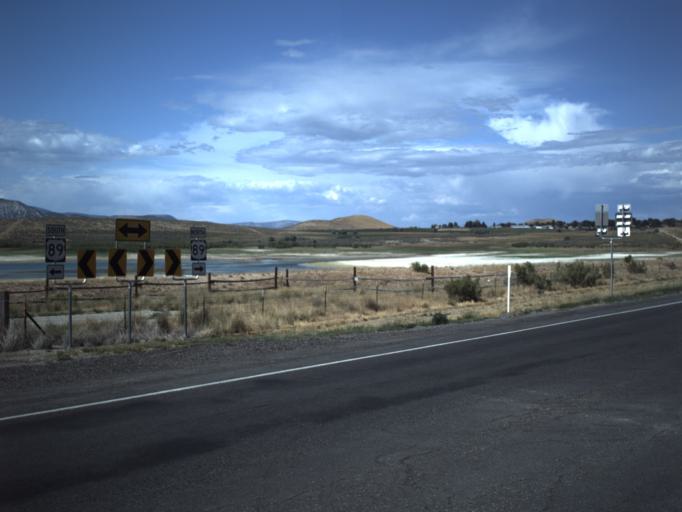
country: US
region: Utah
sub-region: Sanpete County
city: Gunnison
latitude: 39.1716
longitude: -111.7057
